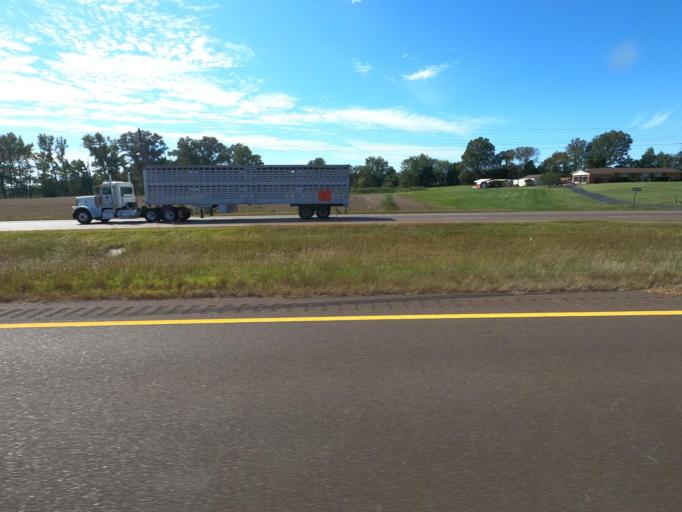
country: US
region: Tennessee
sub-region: Lauderdale County
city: Halls
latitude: 35.9309
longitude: -89.2869
